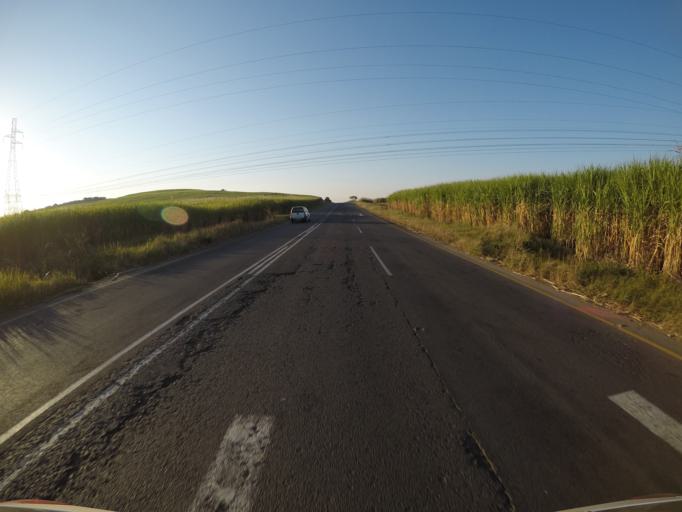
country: ZA
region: KwaZulu-Natal
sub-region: uThungulu District Municipality
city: Eshowe
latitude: -28.9474
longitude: 31.6845
